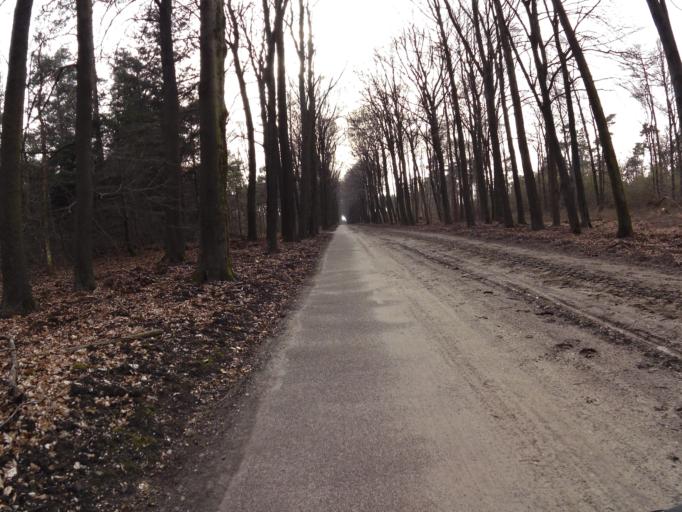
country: NL
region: Gelderland
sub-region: Gemeente Apeldoorn
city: Beekbergen
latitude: 52.1479
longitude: 5.8712
